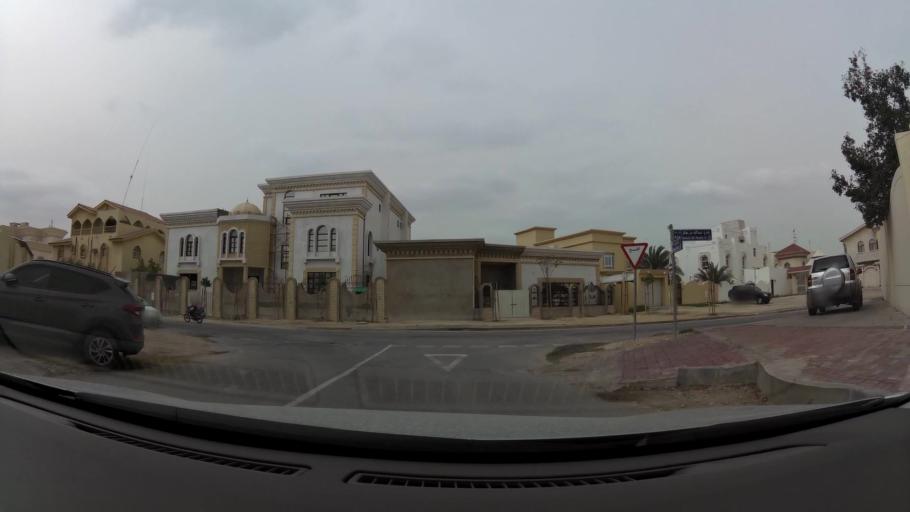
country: QA
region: Baladiyat ad Dawhah
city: Doha
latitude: 25.2476
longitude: 51.5389
